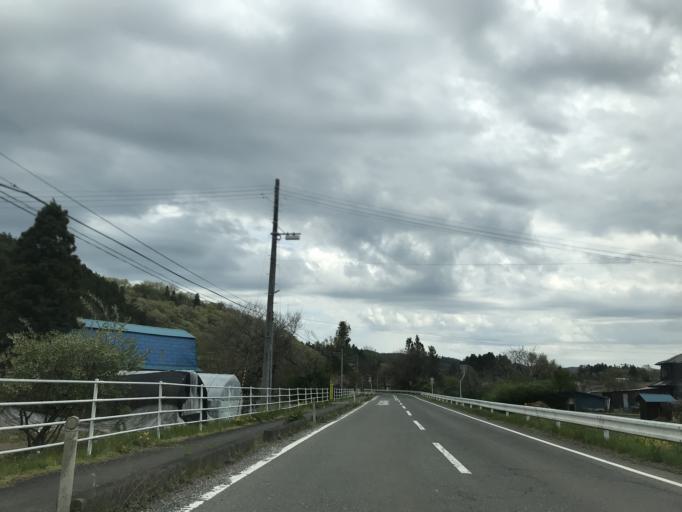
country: JP
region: Iwate
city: Ichinoseki
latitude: 38.7809
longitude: 141.3281
